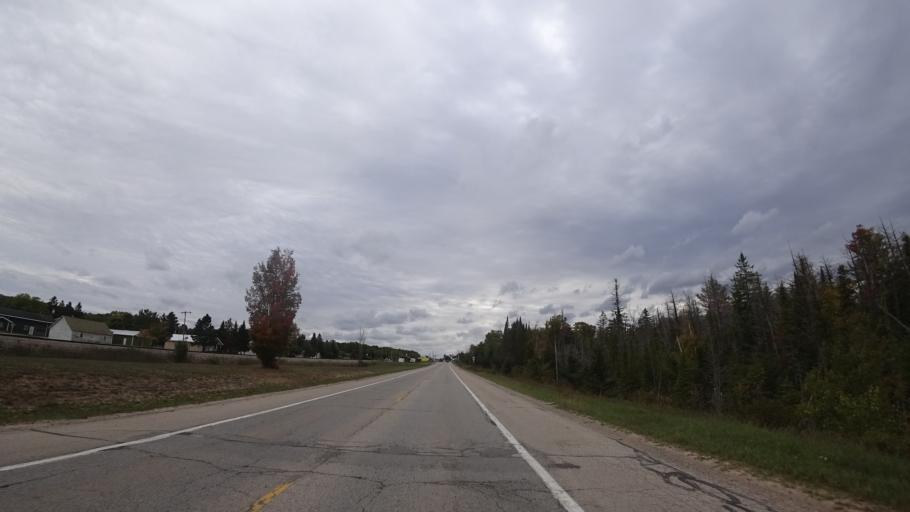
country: US
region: Michigan
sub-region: Charlevoix County
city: Boyne City
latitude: 45.1725
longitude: -84.9148
